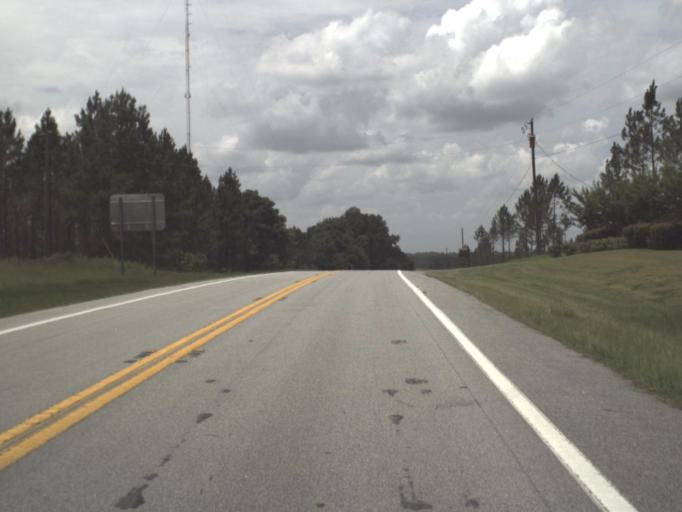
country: US
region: Florida
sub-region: Madison County
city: Madison
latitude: 30.6382
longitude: -83.4455
